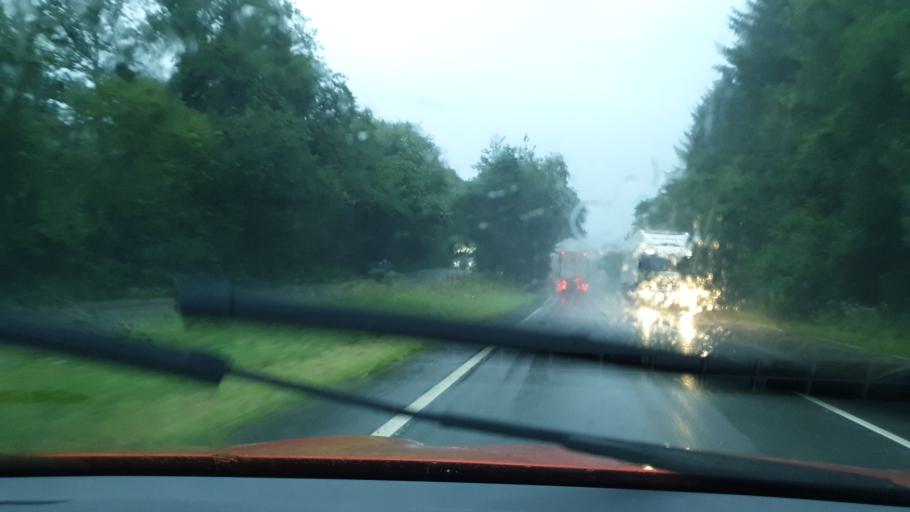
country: GB
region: England
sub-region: Cumbria
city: Ulverston
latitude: 54.2488
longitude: -3.0365
